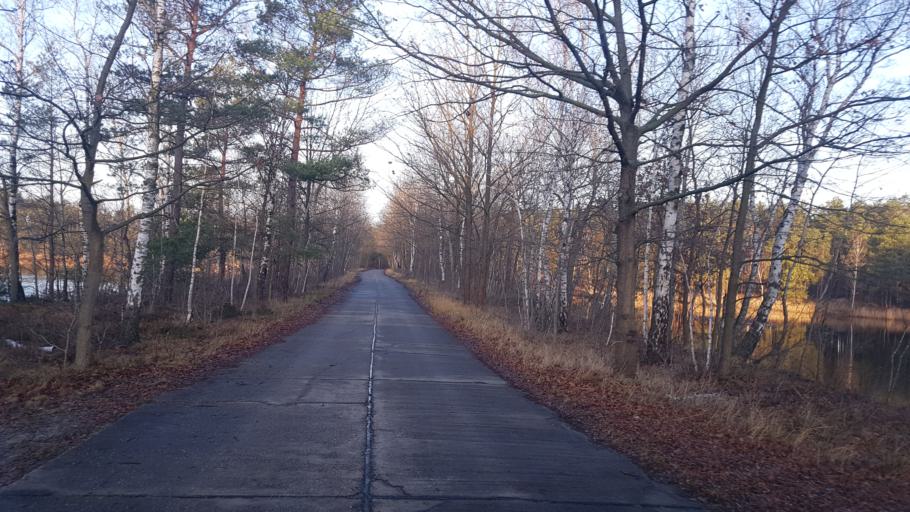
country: DE
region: Brandenburg
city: Ruckersdorf
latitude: 51.5908
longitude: 13.5867
